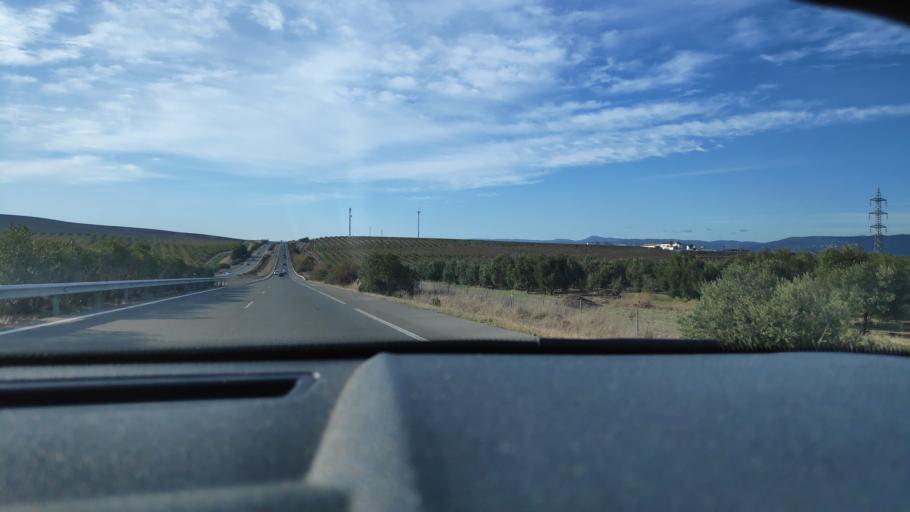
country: ES
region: Andalusia
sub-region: Province of Cordoba
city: Villafranca de Cordoba
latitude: 37.9046
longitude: -4.6194
